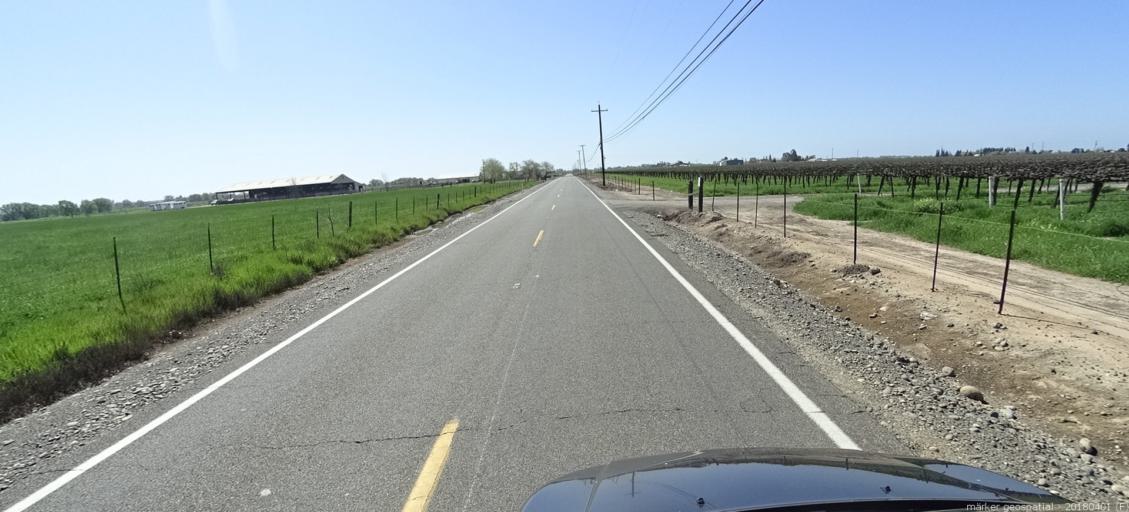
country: US
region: California
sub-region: Sacramento County
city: Herald
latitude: 38.3318
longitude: -121.2238
